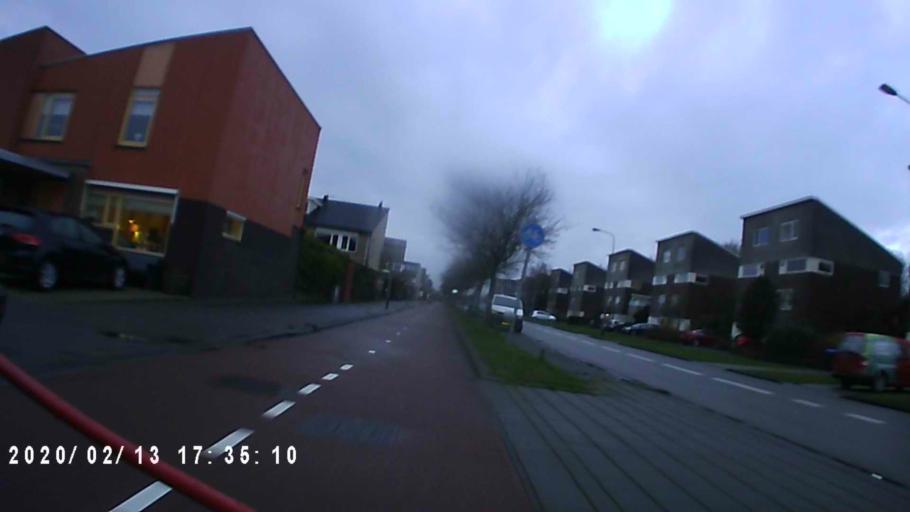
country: NL
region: Groningen
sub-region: Gemeente Groningen
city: Groningen
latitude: 53.2237
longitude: 6.5133
